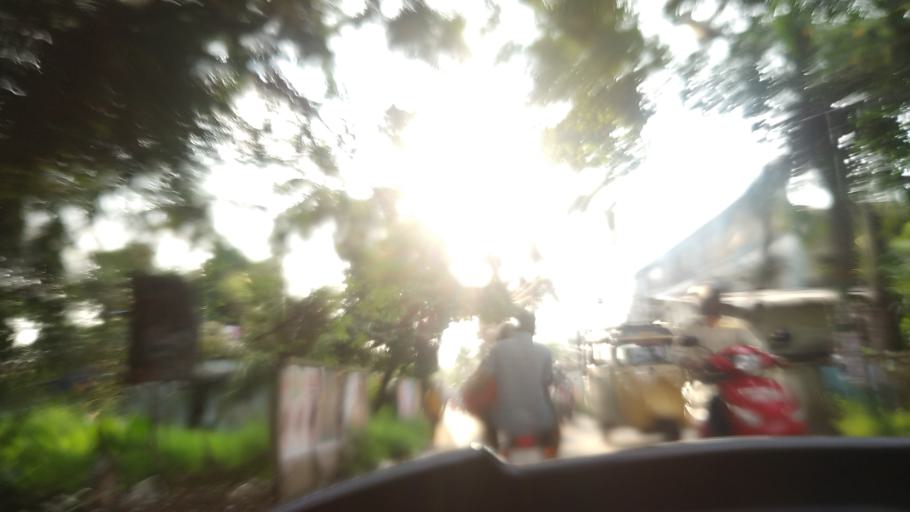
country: IN
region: Kerala
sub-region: Ernakulam
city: Cochin
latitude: 9.9855
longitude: 76.3073
